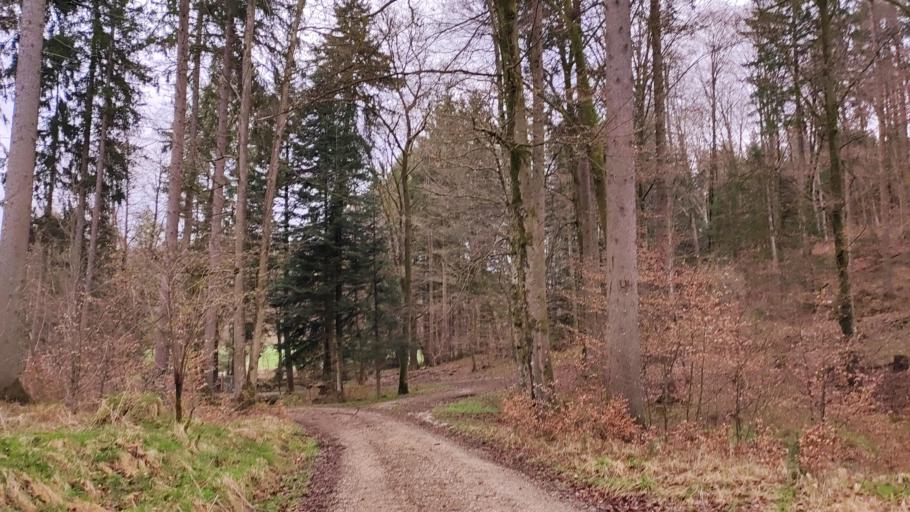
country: DE
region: Bavaria
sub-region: Swabia
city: Landensberg
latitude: 48.4344
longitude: 10.5550
